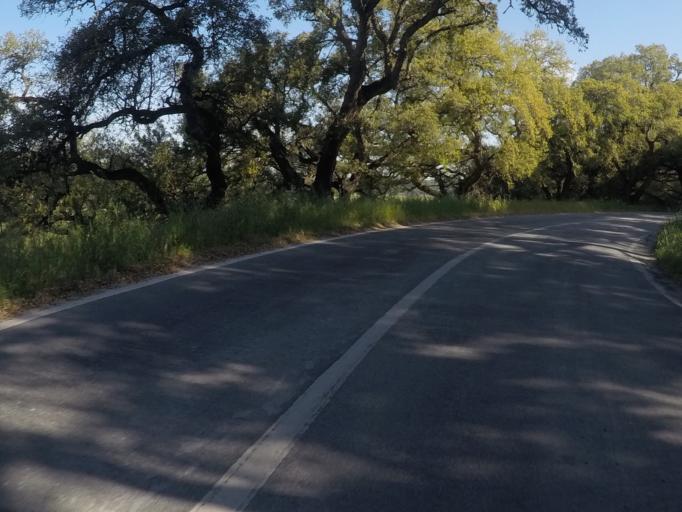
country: PT
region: Setubal
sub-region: Sesimbra
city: Sesimbra
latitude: 38.5049
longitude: -9.1482
